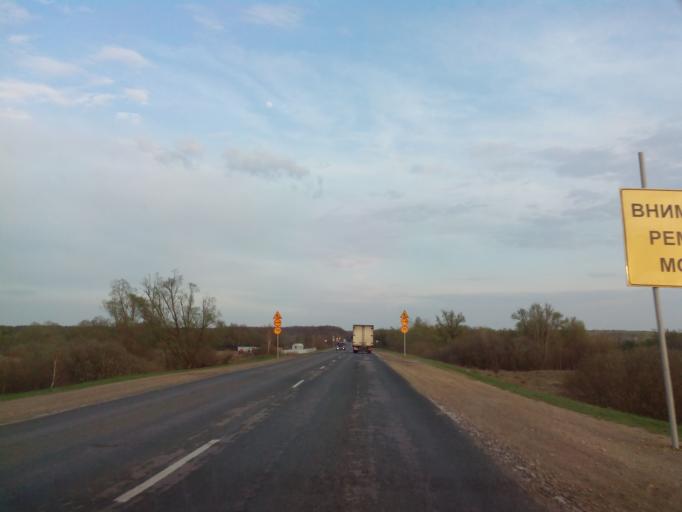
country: RU
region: Rjazan
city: Ryazhsk
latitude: 53.7172
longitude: 39.9191
